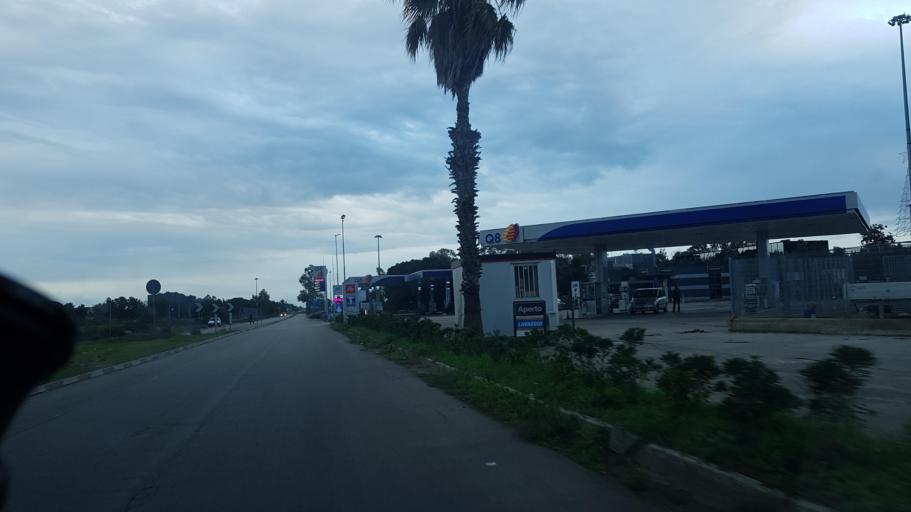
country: IT
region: Apulia
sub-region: Provincia di Lecce
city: Merine
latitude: 40.3449
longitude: 18.2015
